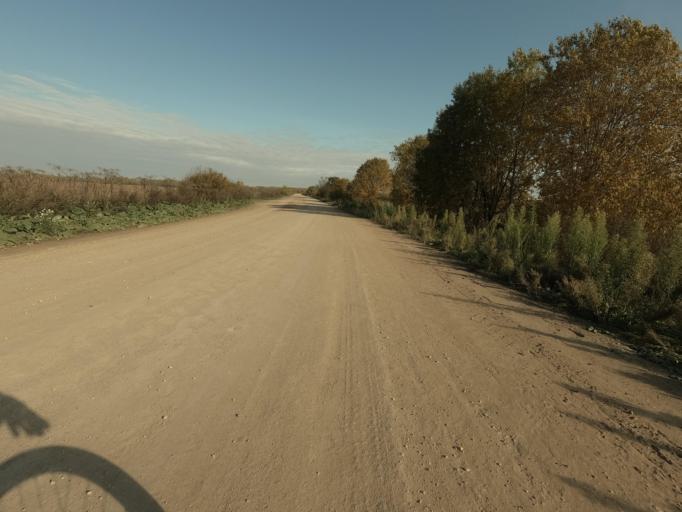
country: RU
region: Novgorod
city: Batetskiy
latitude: 58.8127
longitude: 30.6965
